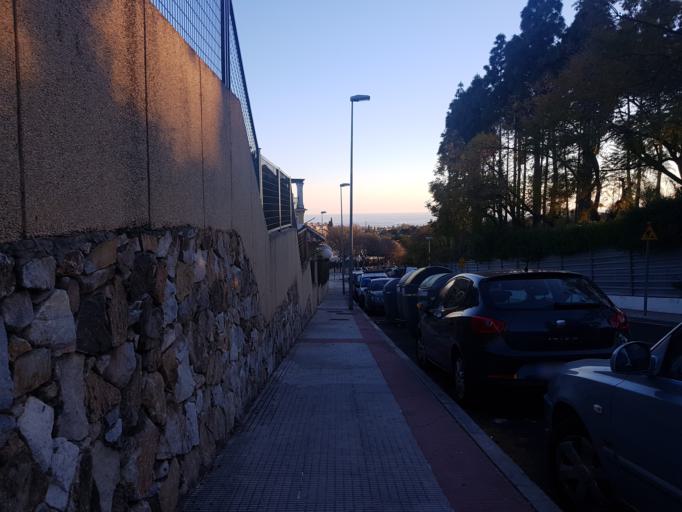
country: ES
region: Andalusia
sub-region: Provincia de Malaga
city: Marbella
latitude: 36.5268
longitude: -4.8900
